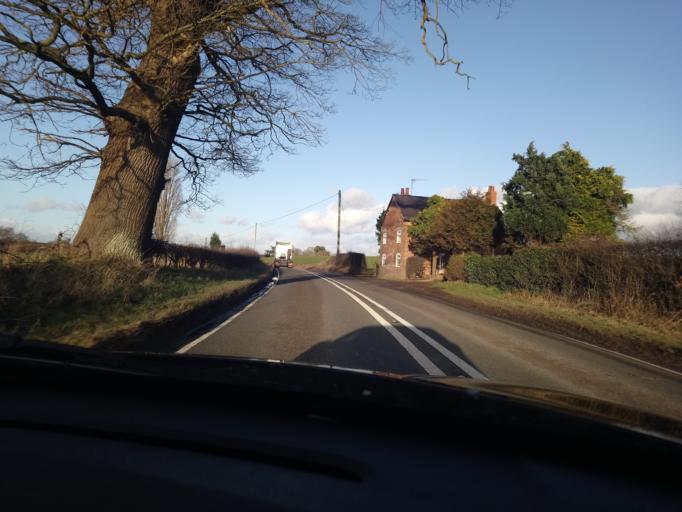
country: GB
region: England
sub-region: Shropshire
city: Ellesmere
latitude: 52.9062
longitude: -2.8494
